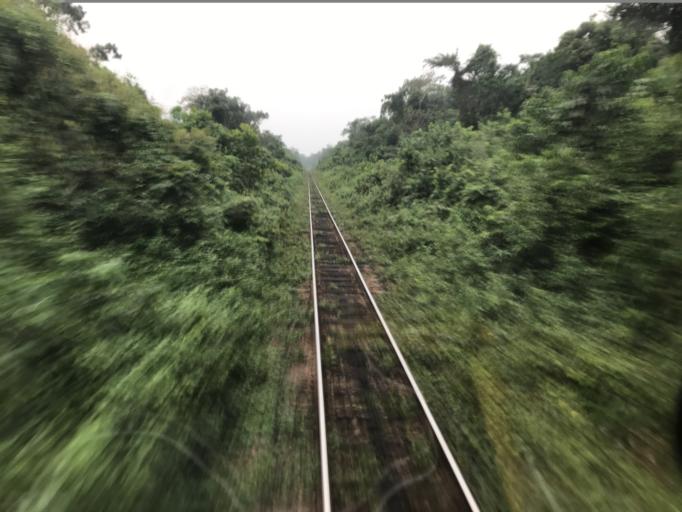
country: CM
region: Littoral
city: Edea
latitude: 3.9562
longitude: 10.0860
